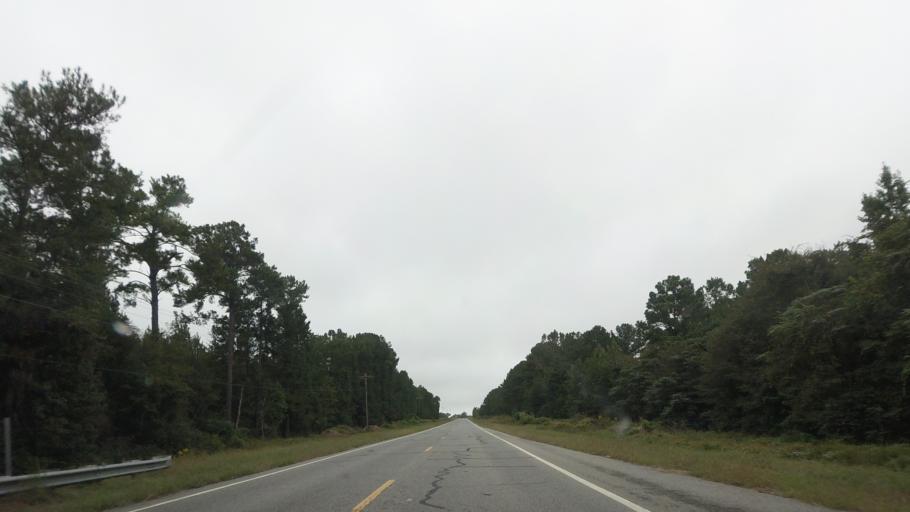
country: US
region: Georgia
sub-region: Irwin County
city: Ocilla
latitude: 31.5007
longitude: -83.2387
